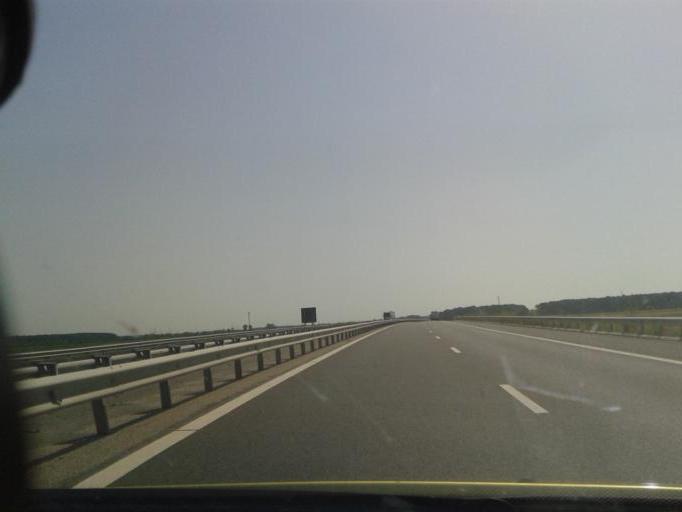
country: RO
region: Prahova
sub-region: Comuna Berceni
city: Corlatesti
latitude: 44.8886
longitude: 26.1052
